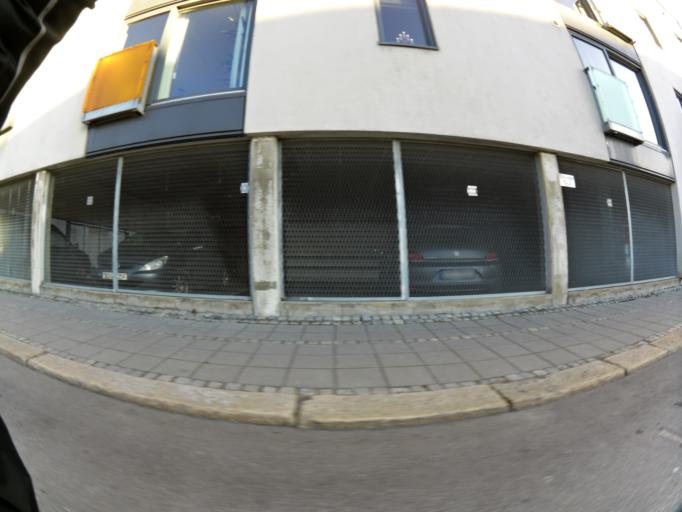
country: NO
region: Ostfold
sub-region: Fredrikstad
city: Fredrikstad
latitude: 59.2082
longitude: 10.9403
